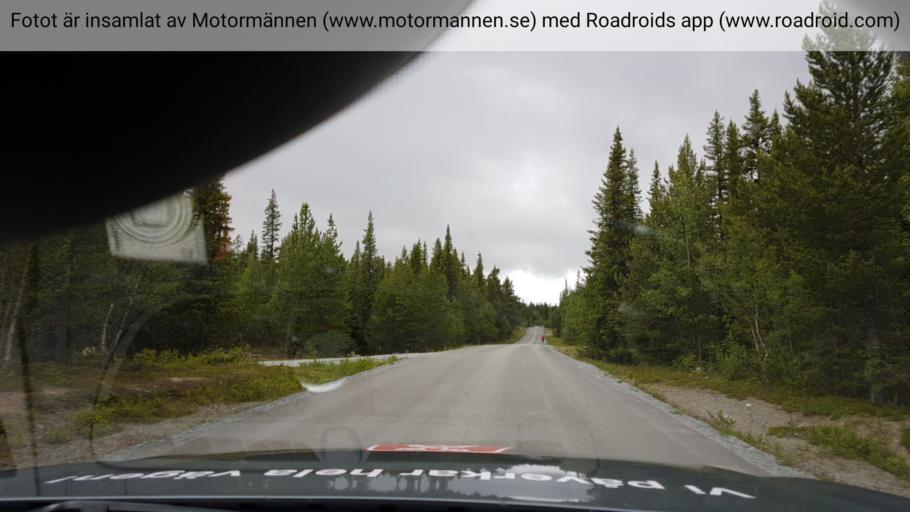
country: SE
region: Jaemtland
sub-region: Are Kommun
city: Are
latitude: 62.8637
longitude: 12.7634
